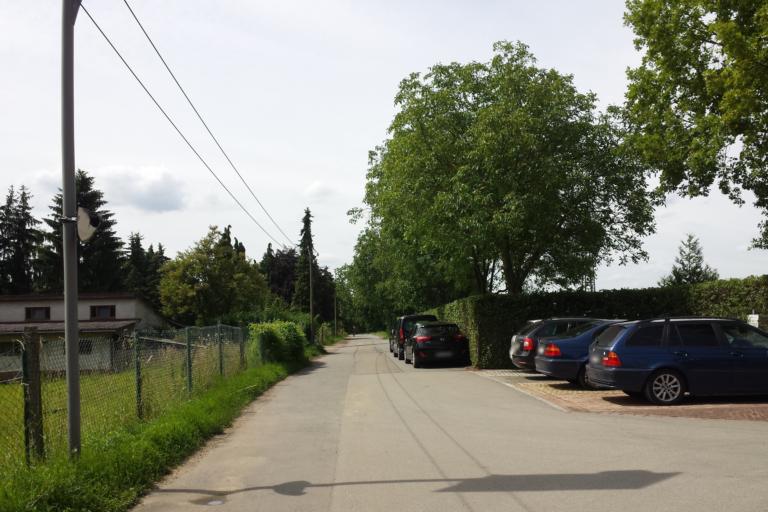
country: DE
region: Baden-Wuerttemberg
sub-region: Karlsruhe Region
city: Dossenheim
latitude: 49.4397
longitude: 8.6466
